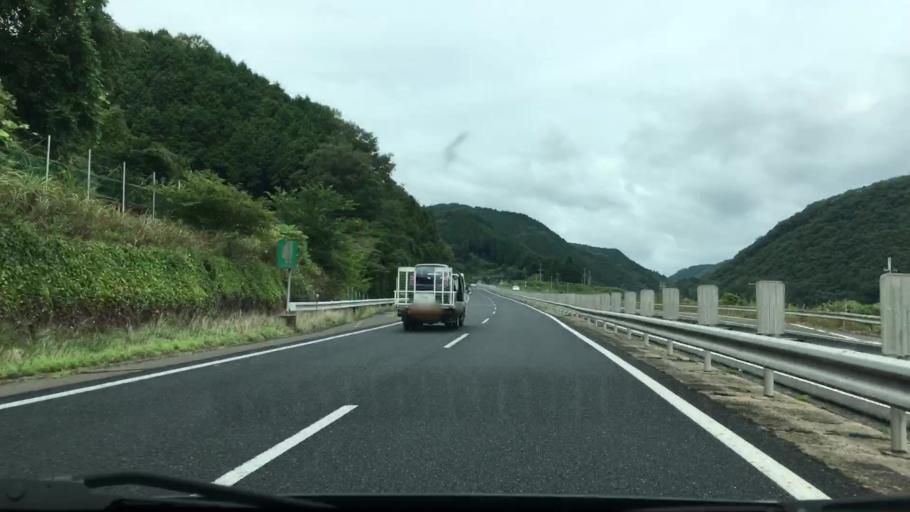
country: JP
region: Hyogo
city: Yamazakicho-nakabirose
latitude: 35.0111
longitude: 134.3020
